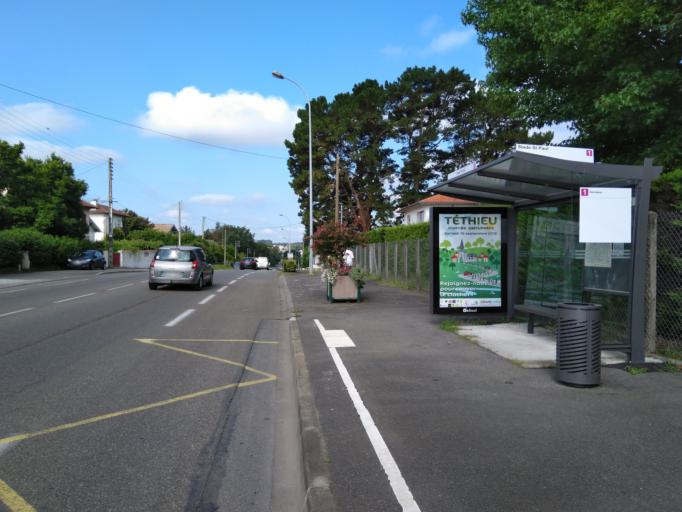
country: FR
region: Aquitaine
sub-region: Departement des Landes
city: Saint-Paul-les-Dax
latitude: 43.7248
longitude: -1.0603
